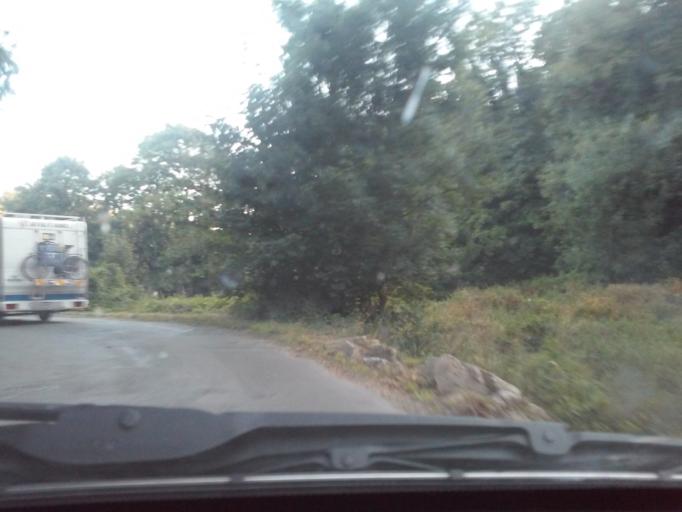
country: FR
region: Brittany
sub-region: Departement des Cotes-d'Armor
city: Lanvallay
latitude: 48.4624
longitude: -2.0325
